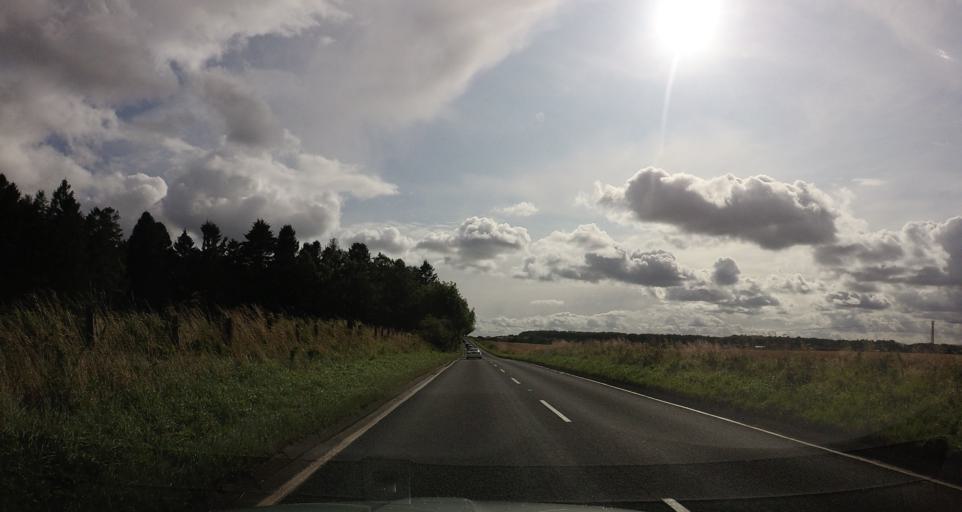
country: GB
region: Scotland
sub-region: Clackmannanshire
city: Clackmannan
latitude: 56.1054
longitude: -3.7152
